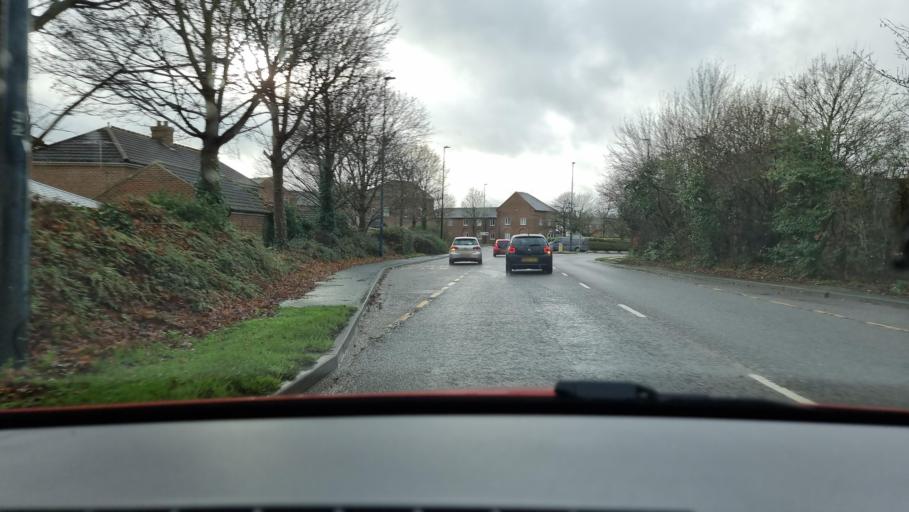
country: GB
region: England
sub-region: Buckinghamshire
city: Aylesbury
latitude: 51.8146
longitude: -0.8371
